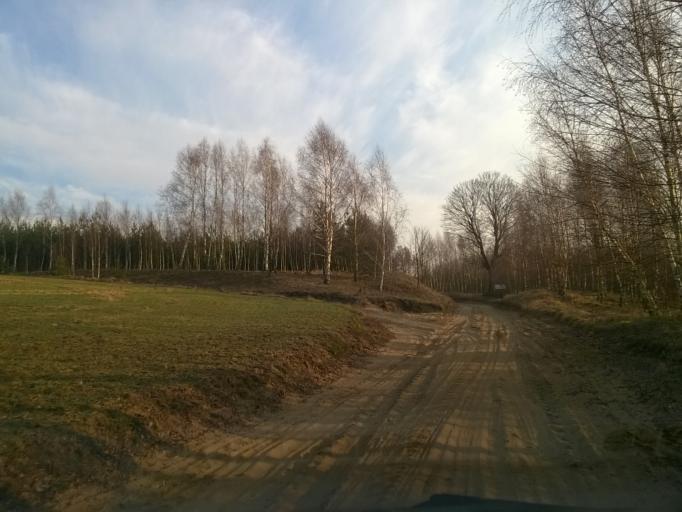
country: PL
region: Kujawsko-Pomorskie
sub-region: Powiat tucholski
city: Kesowo
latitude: 53.5074
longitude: 17.7045
